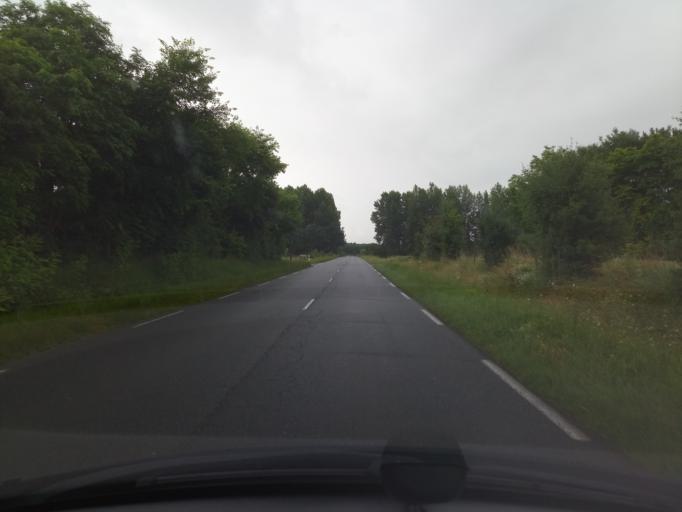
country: FR
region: Poitou-Charentes
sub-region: Departement de la Charente-Maritime
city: Courcon
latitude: 46.1682
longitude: -0.8370
